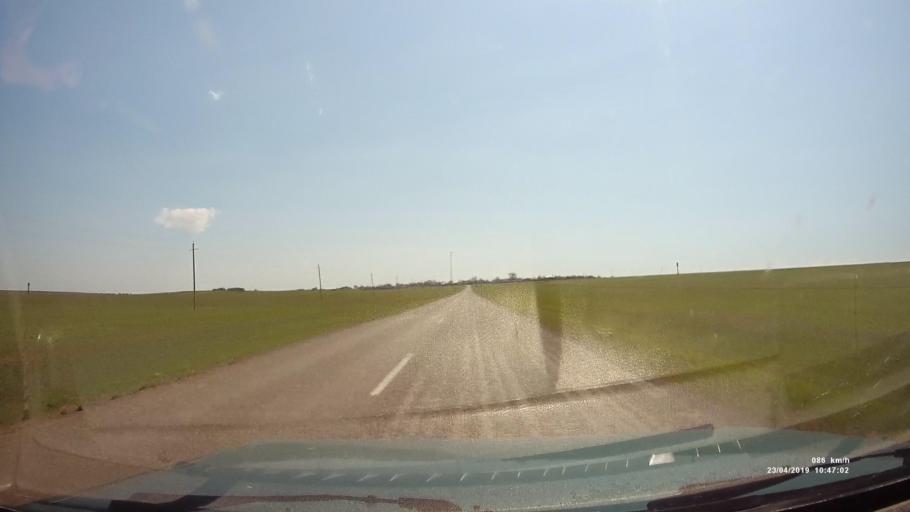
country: RU
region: Kalmykiya
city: Yashalta
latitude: 46.4382
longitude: 42.7008
